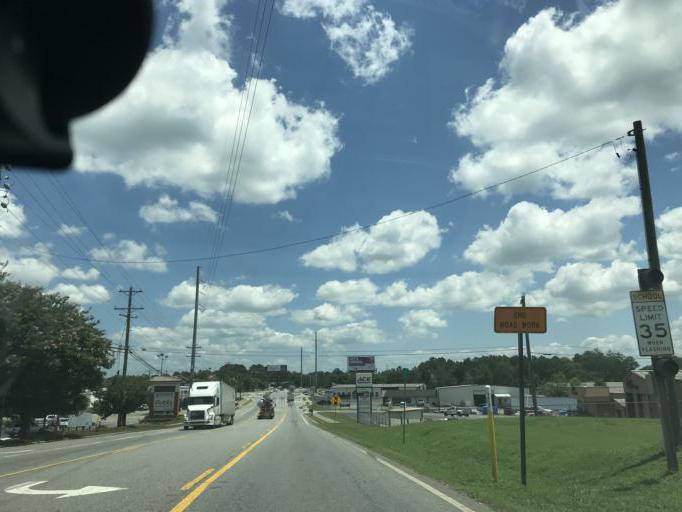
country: US
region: Georgia
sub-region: Fulton County
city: Milton
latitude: 34.1579
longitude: -84.2393
